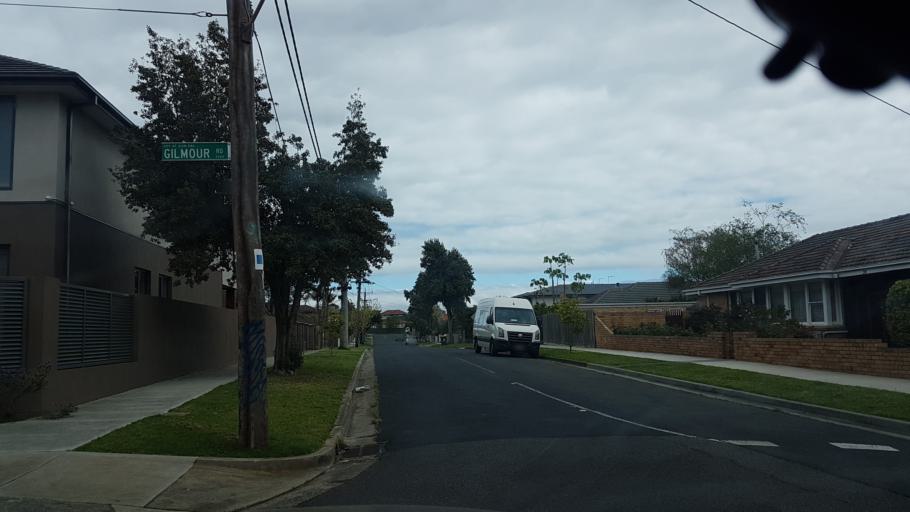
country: AU
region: Victoria
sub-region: Bayside
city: Moorabbin
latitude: -37.9303
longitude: 145.0422
